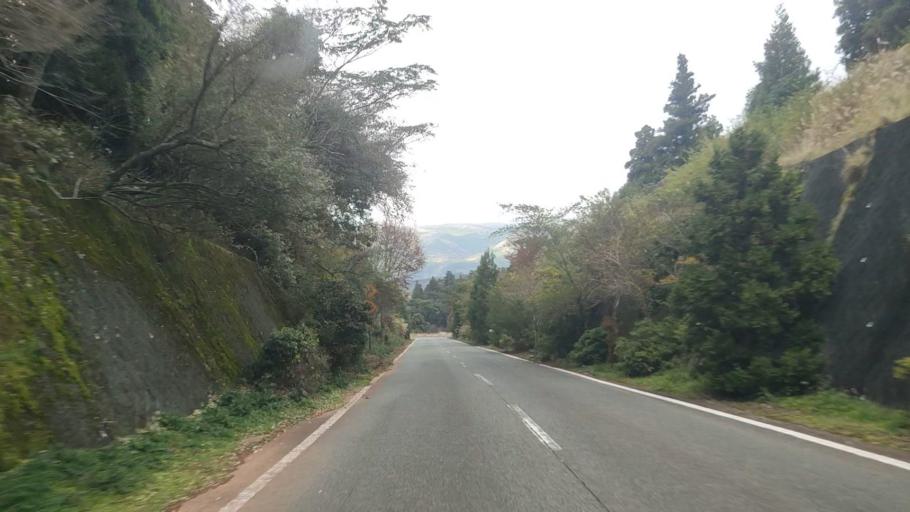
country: JP
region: Shizuoka
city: Heda
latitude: 34.8977
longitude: 138.8464
